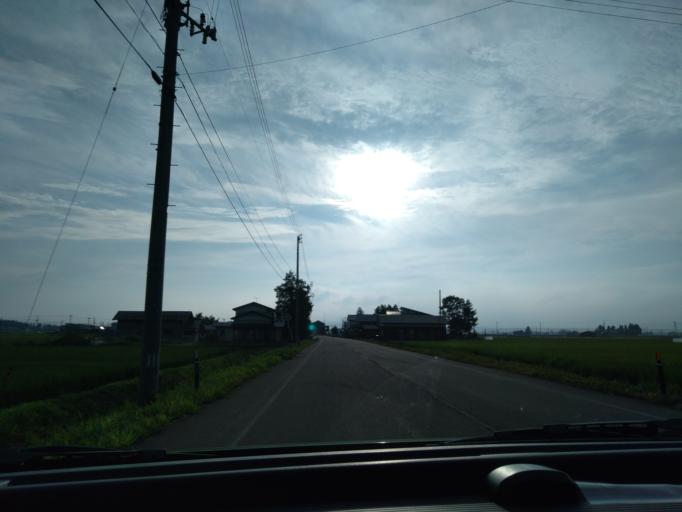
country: JP
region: Akita
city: Yokotemachi
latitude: 39.3746
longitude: 140.5388
